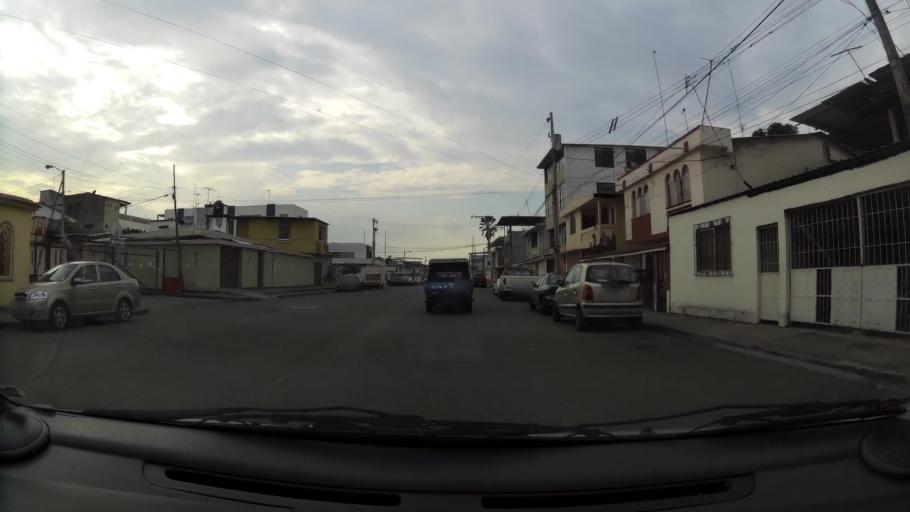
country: EC
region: Guayas
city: Guayaquil
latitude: -2.2482
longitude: -79.8974
